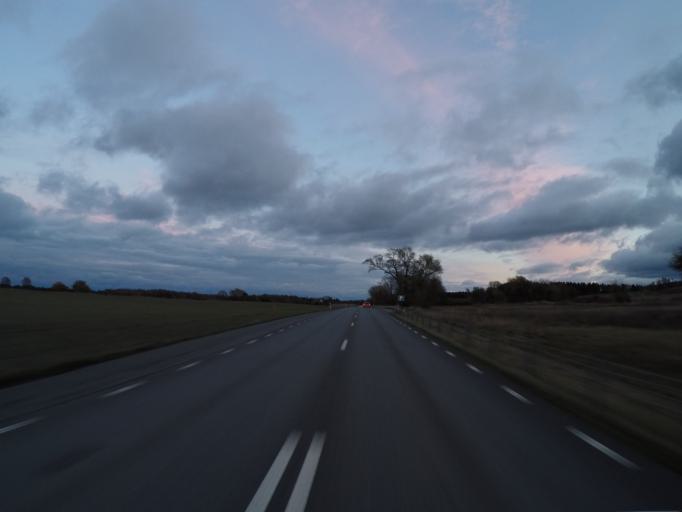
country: SE
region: Skane
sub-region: Kristianstads Kommun
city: Degeberga
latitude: 55.8209
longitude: 14.1194
